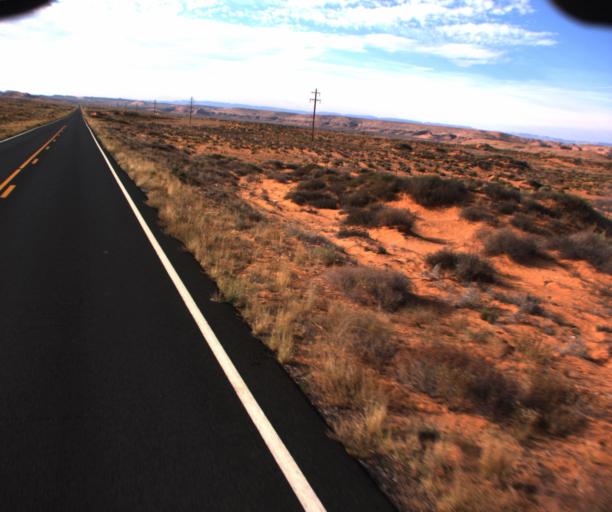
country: US
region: Arizona
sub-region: Apache County
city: Many Farms
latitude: 36.8239
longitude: -109.6448
